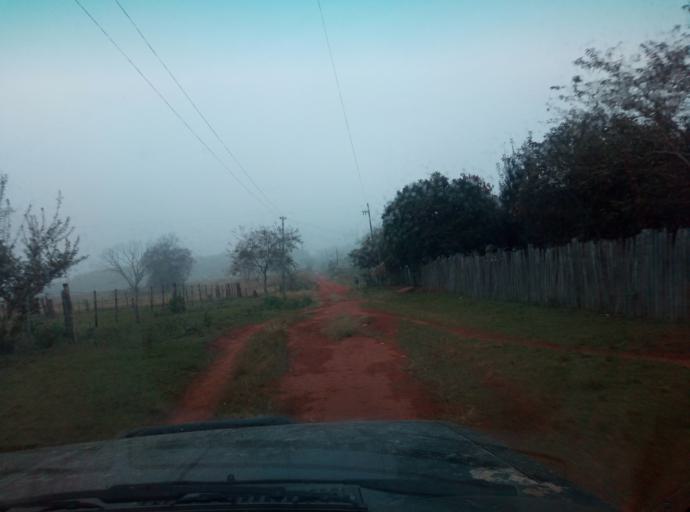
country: PY
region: Caaguazu
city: Doctor Cecilio Baez
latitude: -25.1589
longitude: -56.2616
